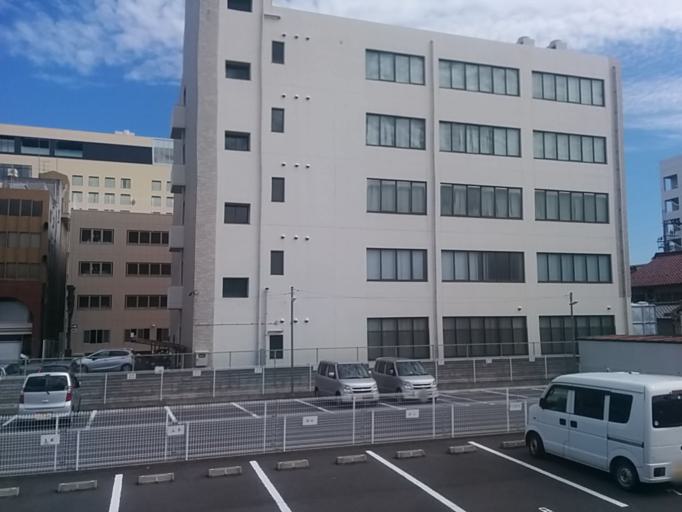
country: JP
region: Nara
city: Kashihara-shi
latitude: 34.5114
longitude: 135.7912
